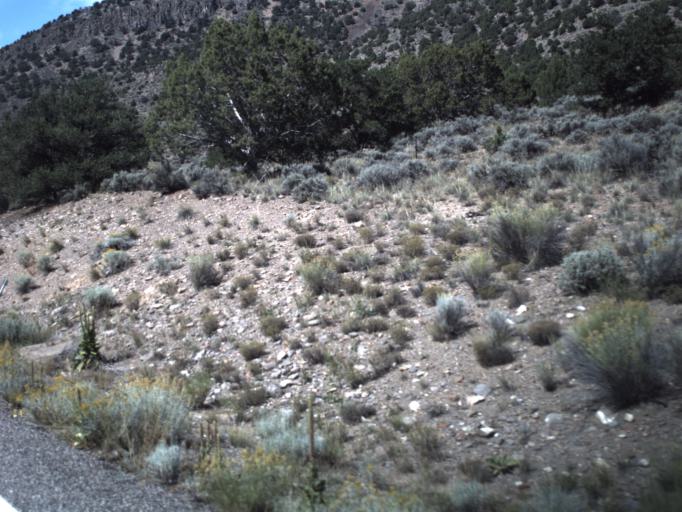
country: US
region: Utah
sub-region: Piute County
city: Junction
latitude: 38.2583
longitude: -112.2715
